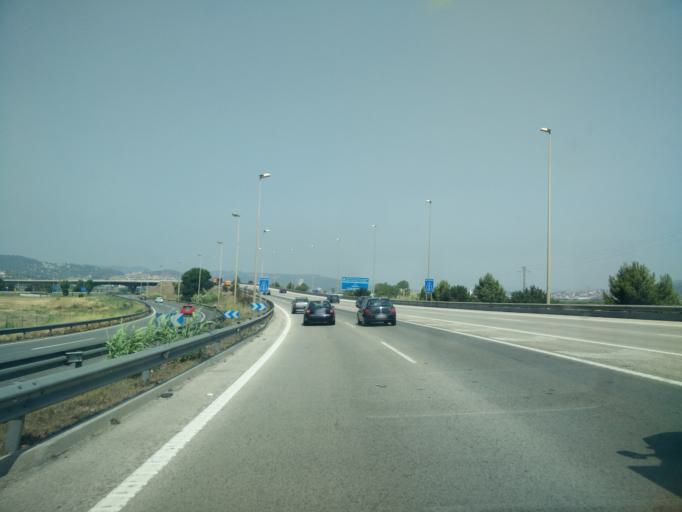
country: ES
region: Catalonia
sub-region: Provincia de Barcelona
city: Sant Feliu de Llobregat
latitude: 41.3758
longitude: 2.0369
